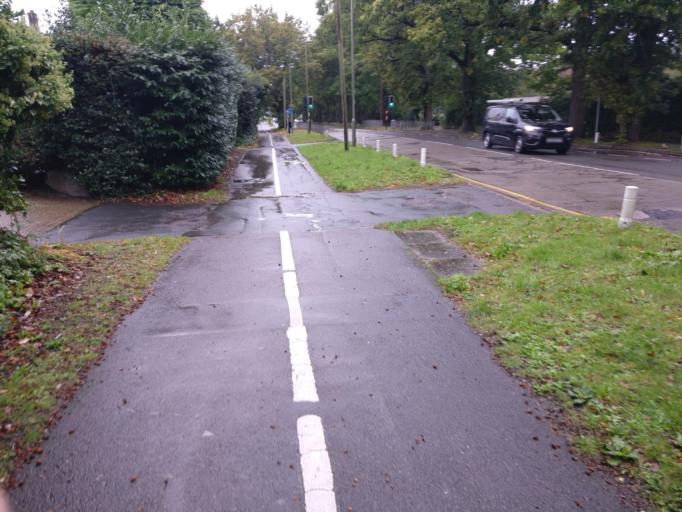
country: GB
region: England
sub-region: Surrey
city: Frimley
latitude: 51.3196
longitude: -0.7347
